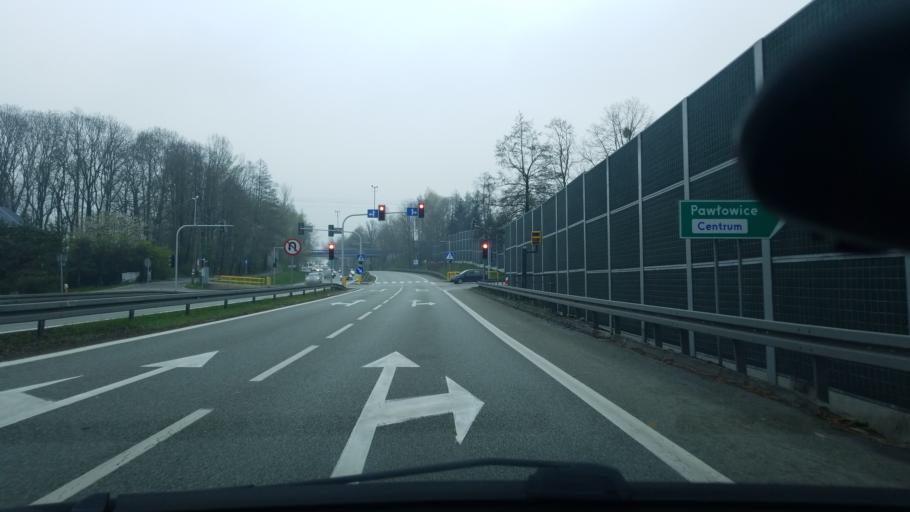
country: PL
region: Silesian Voivodeship
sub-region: Powiat pszczynski
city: Pawlowice
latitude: 49.9677
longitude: 18.7189
